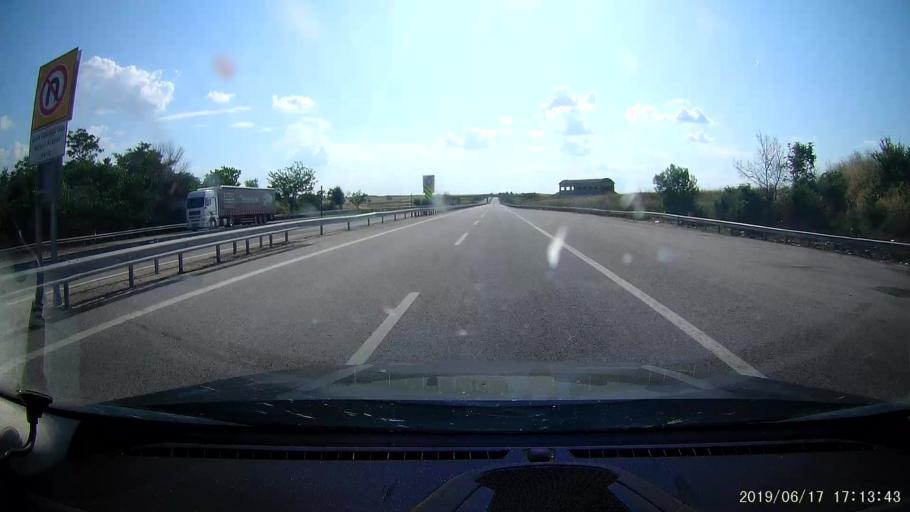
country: TR
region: Edirne
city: Edirne
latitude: 41.7005
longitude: 26.5345
